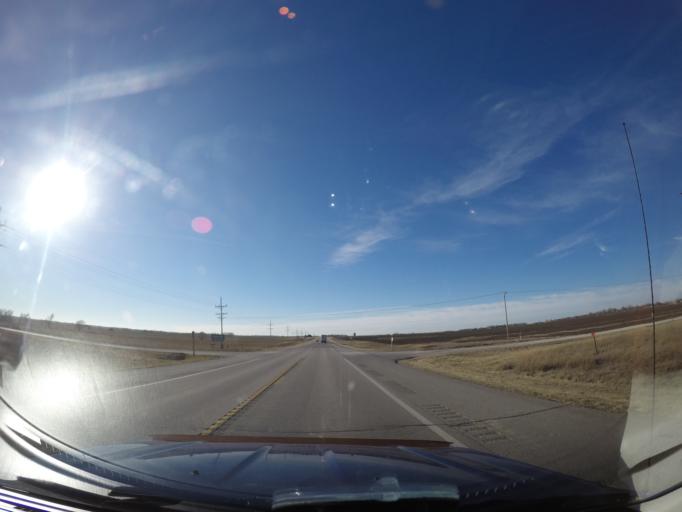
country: US
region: Kansas
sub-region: Marion County
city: Hillsboro
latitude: 38.3622
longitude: -97.2978
